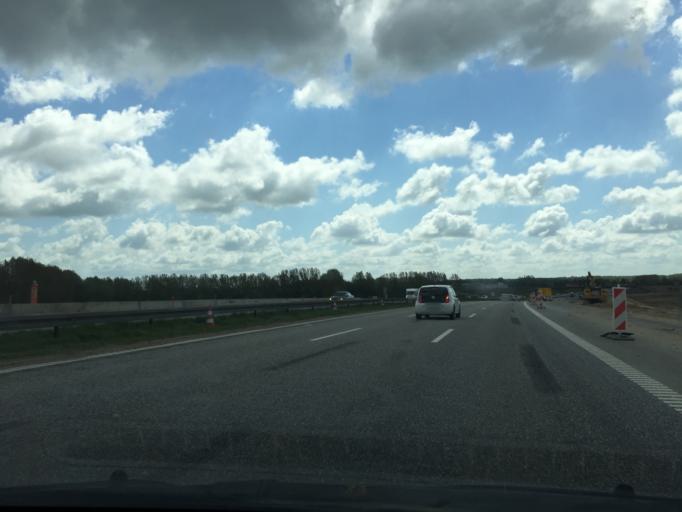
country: DK
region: Zealand
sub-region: Koge Kommune
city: Koge
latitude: 55.4903
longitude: 12.1689
